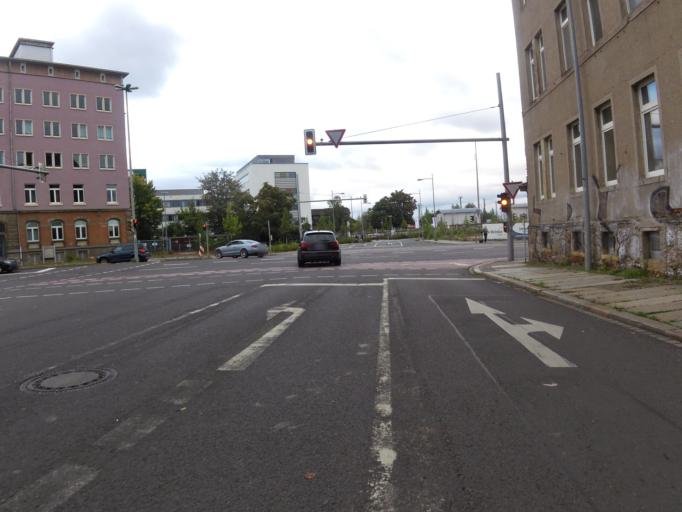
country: DE
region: Saxony
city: Leipzig
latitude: 51.3460
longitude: 12.3886
